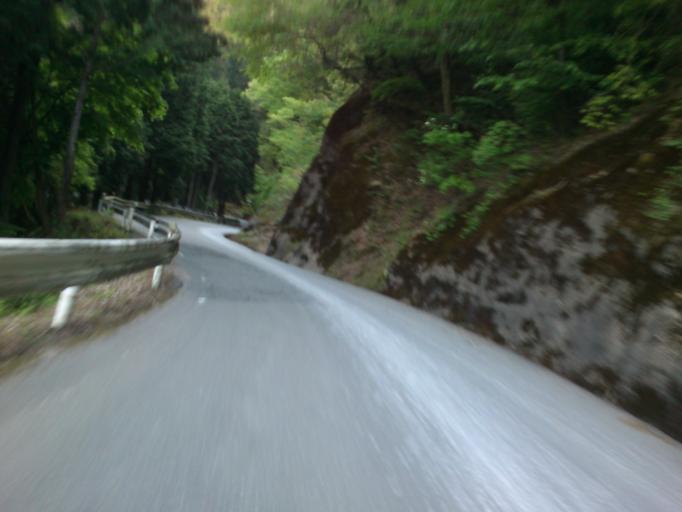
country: JP
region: Kyoto
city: Fukuchiyama
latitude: 35.2536
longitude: 135.0664
